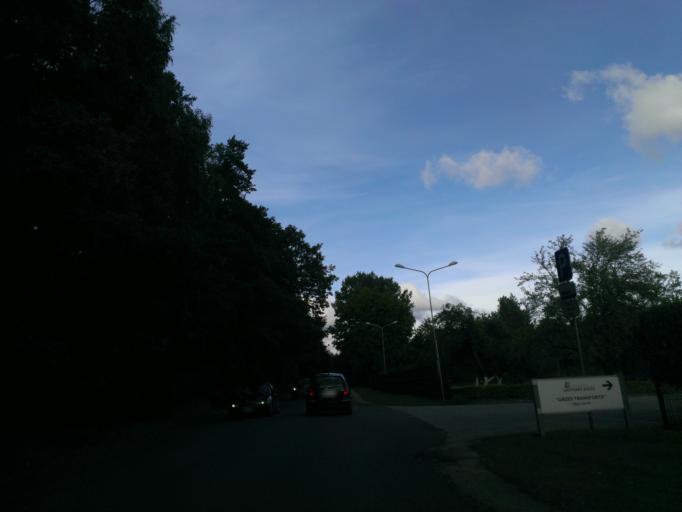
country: LV
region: Stopini
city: Ulbroka
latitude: 56.9576
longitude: 24.2235
